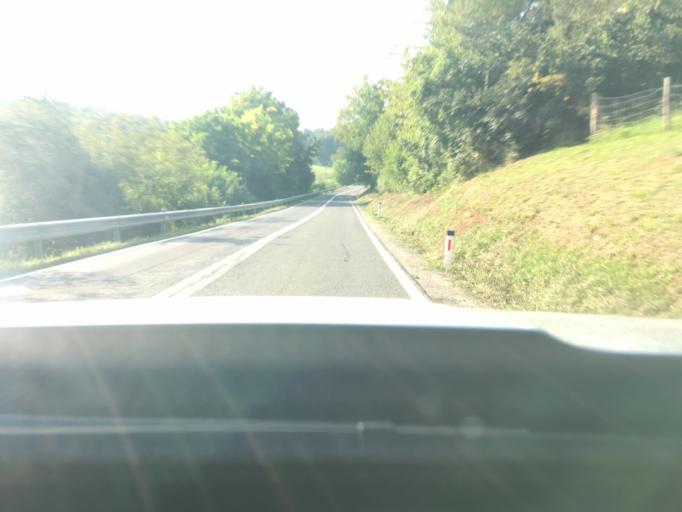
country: SI
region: Metlika
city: Metlika
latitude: 45.6549
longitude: 15.2970
